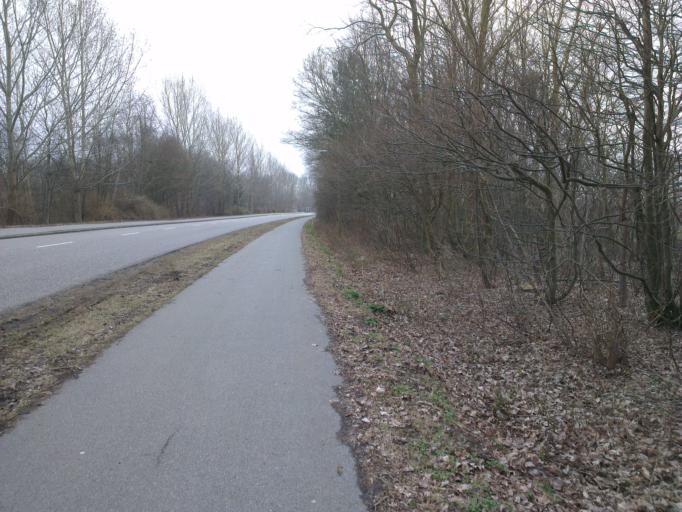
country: DK
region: Capital Region
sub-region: Frederikssund Kommune
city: Frederikssund
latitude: 55.8229
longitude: 12.0913
